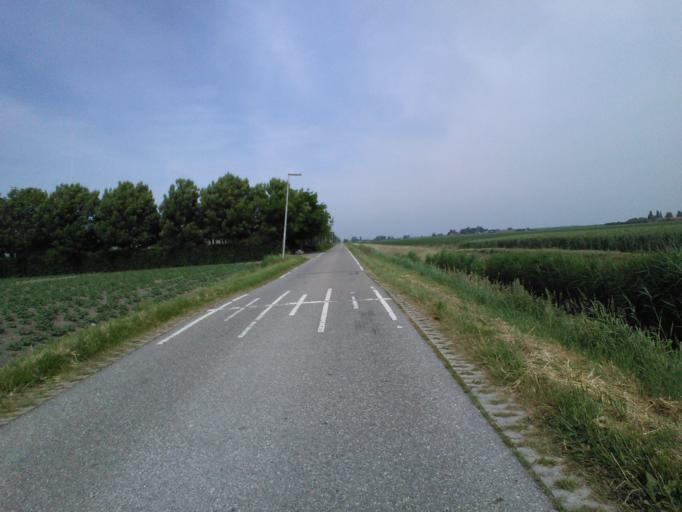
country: NL
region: South Holland
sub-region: Gemeente Waddinxveen
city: Groenswaard
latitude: 52.0376
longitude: 4.6201
